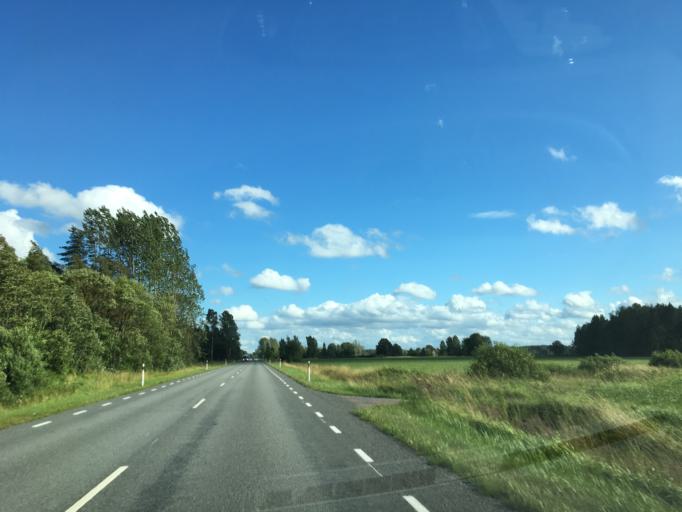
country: EE
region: Paernumaa
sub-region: Vaendra vald (alev)
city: Vandra
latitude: 58.5890
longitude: 25.1646
